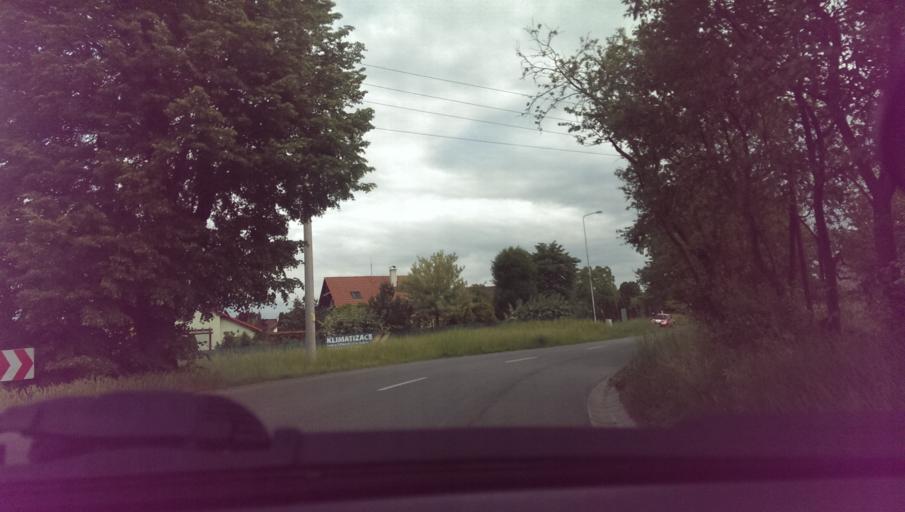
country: CZ
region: Zlin
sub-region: Okres Kromeriz
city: Kromeriz
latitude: 49.2842
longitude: 17.4024
